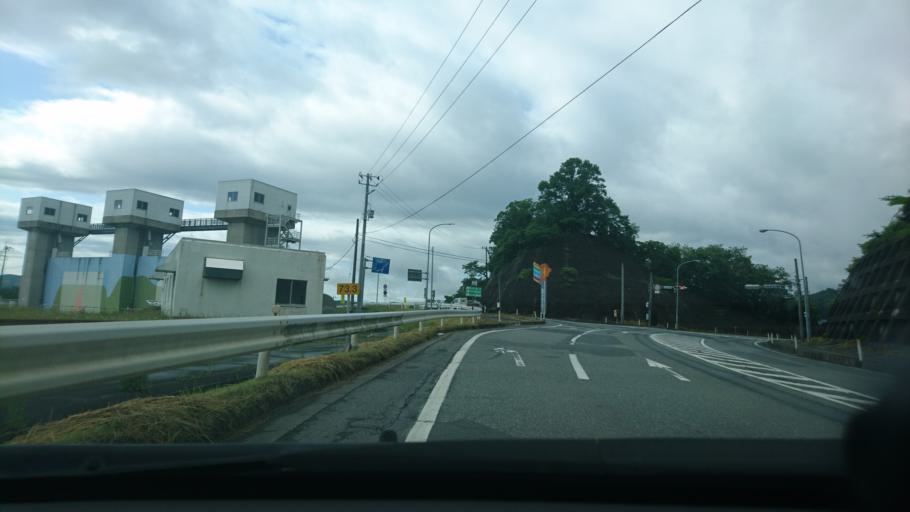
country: JP
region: Miyagi
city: Wakuya
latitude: 38.6026
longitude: 141.3024
